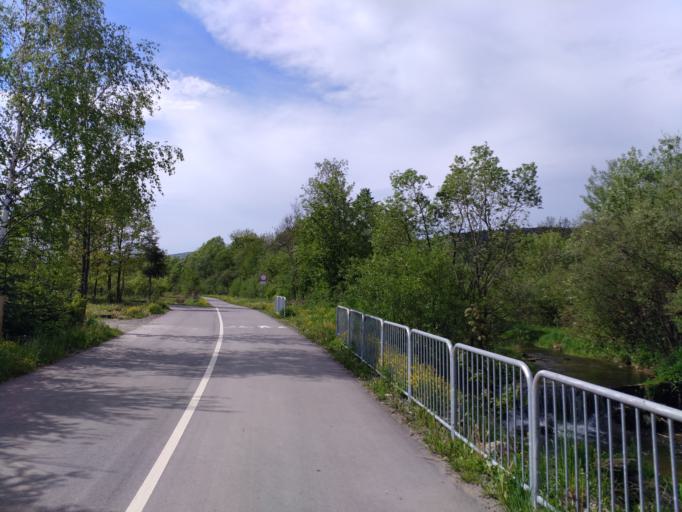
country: PL
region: Lesser Poland Voivodeship
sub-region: Powiat nowosadecki
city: Lacko
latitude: 49.5700
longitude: 20.4278
